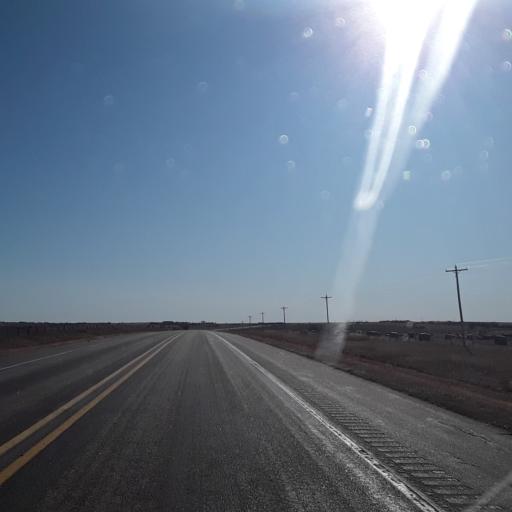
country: US
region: Nebraska
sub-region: Frontier County
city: Stockville
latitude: 40.5763
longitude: -100.6298
